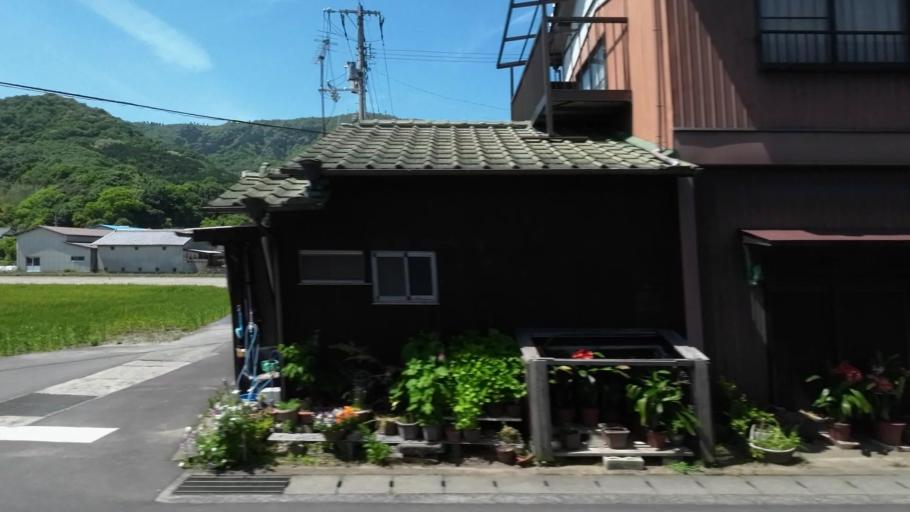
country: JP
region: Kagawa
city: Marugame
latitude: 34.2104
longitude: 133.8036
